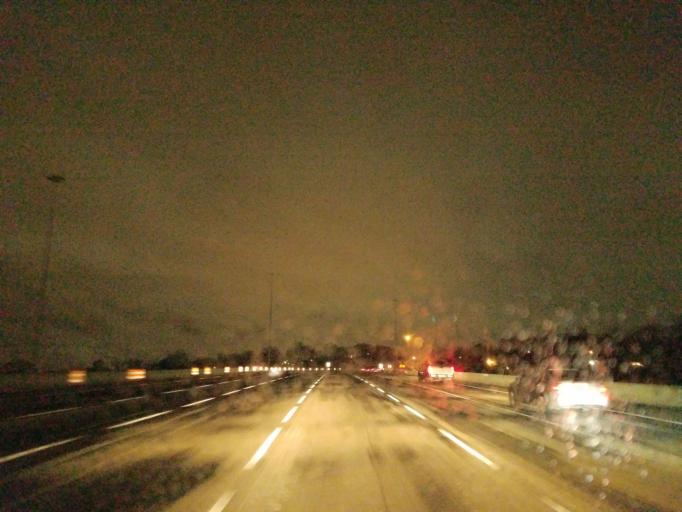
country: US
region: Alabama
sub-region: Jefferson County
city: Birmingham
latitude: 33.5206
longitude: -86.8308
